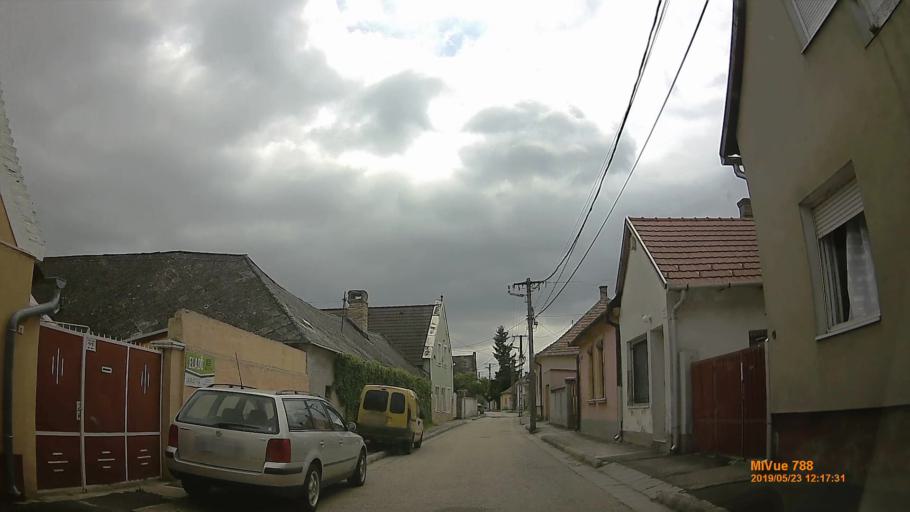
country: HU
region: Veszprem
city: Veszprem
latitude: 47.1007
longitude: 17.8949
